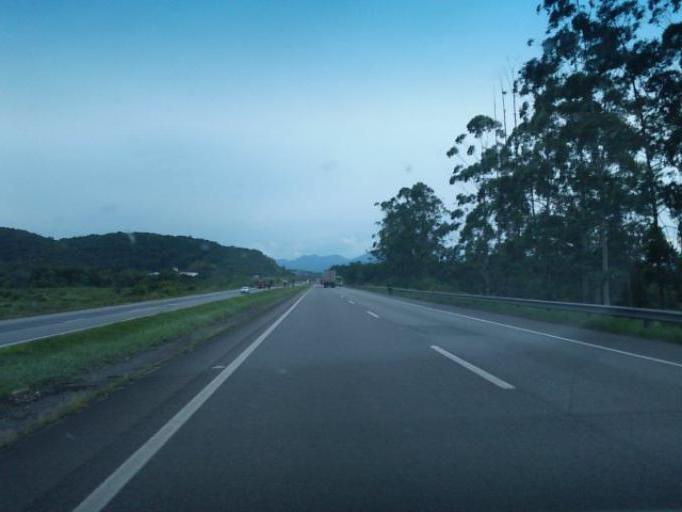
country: BR
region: Sao Paulo
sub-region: Jacupiranga
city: Jacupiranga
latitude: -24.6817
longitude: -47.9844
